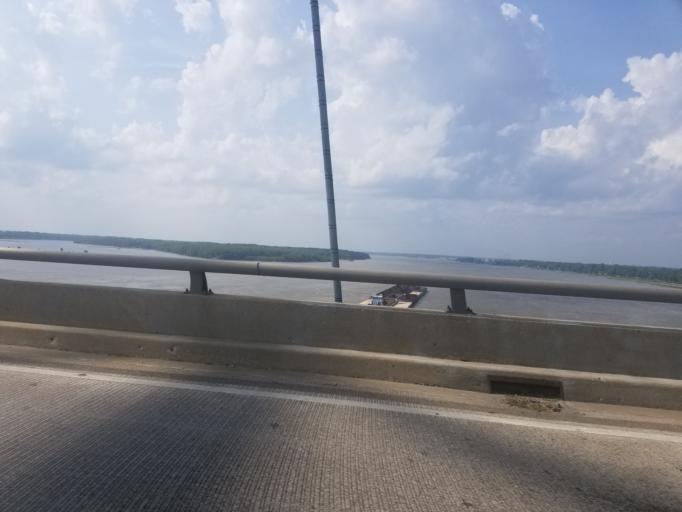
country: US
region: Tennessee
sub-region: Shelby County
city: Memphis
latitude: 35.1532
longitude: -90.0619
